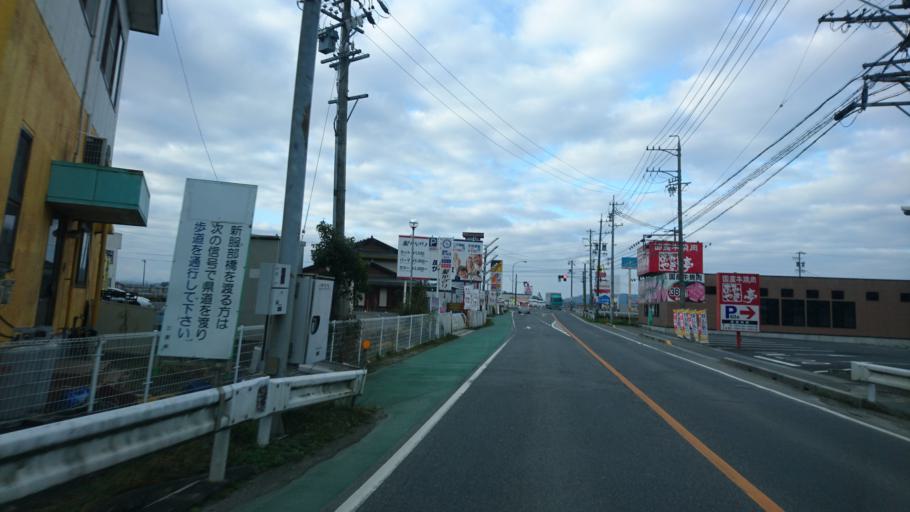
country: JP
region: Mie
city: Ueno-ebisumachi
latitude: 34.7810
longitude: 136.1347
